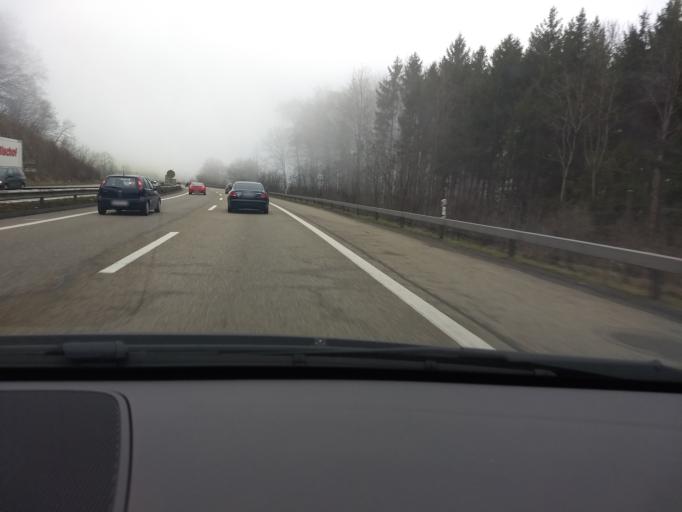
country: CH
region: Basel-Landschaft
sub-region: Bezirk Liestal
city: Arisdorf
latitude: 47.4949
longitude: 7.7698
